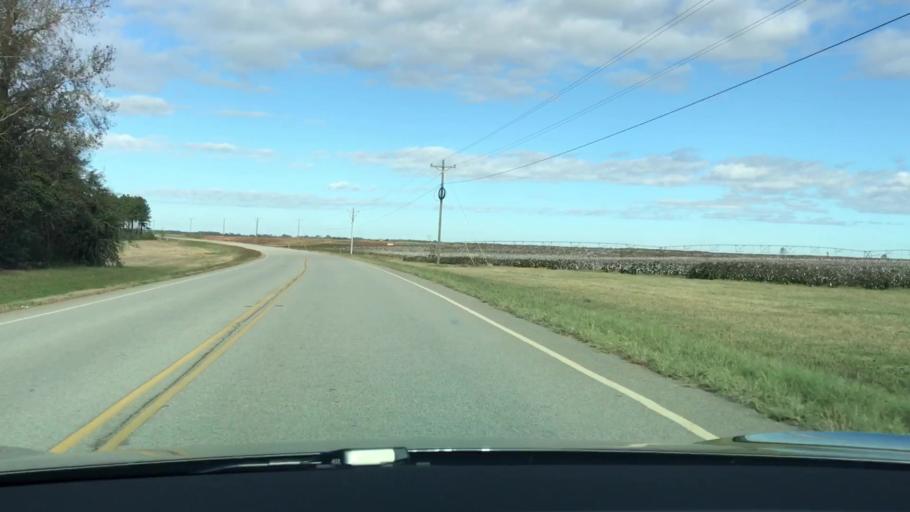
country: US
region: Georgia
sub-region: Jefferson County
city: Wrens
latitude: 33.1095
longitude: -82.4272
